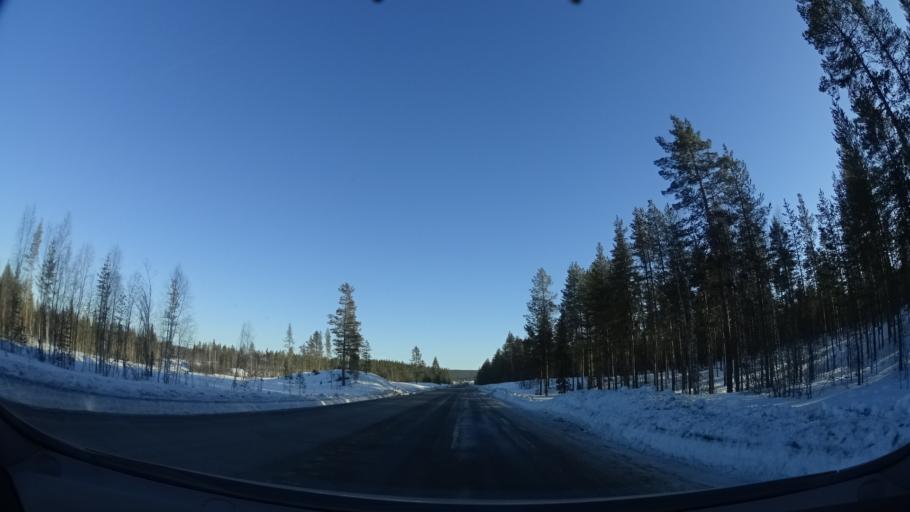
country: SE
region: Vaesterbotten
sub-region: Skelleftea Kommun
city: Langsele
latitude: 65.0436
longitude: 20.0773
